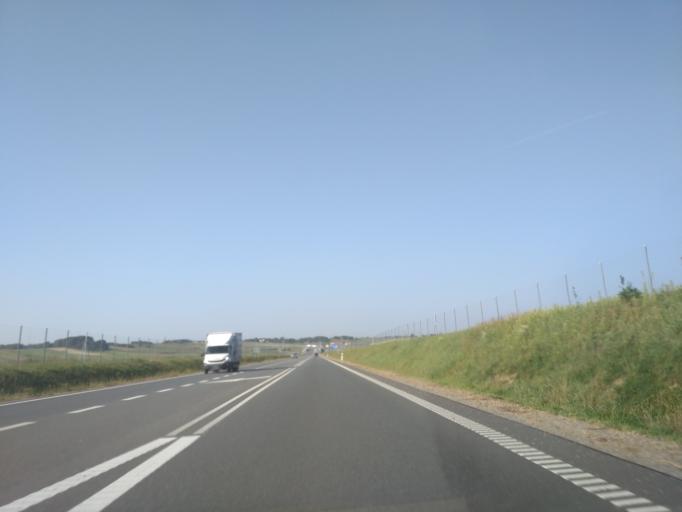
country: PL
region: Subcarpathian Voivodeship
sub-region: Powiat rzeszowski
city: Sokolow Malopolski
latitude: 50.2124
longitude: 22.1206
